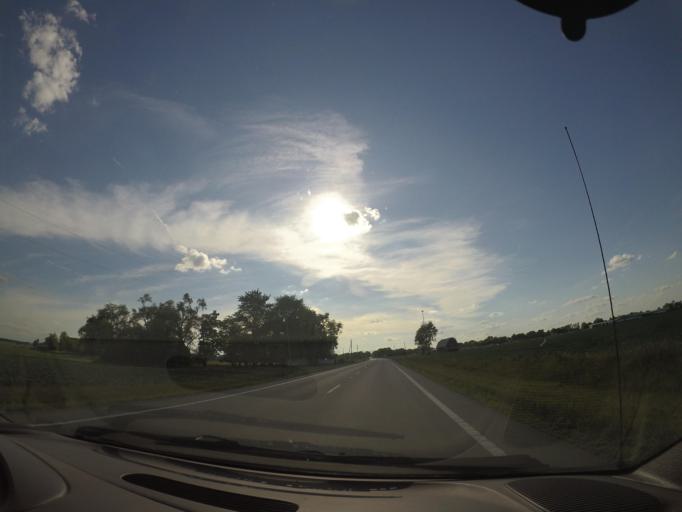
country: US
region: Ohio
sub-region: Fulton County
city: Archbold
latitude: 41.4356
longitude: -84.2426
